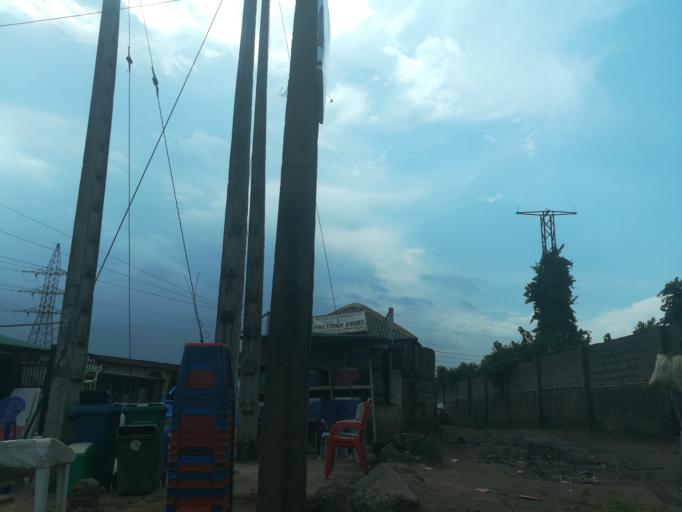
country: NG
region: Lagos
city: Ikorodu
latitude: 6.6258
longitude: 3.5057
